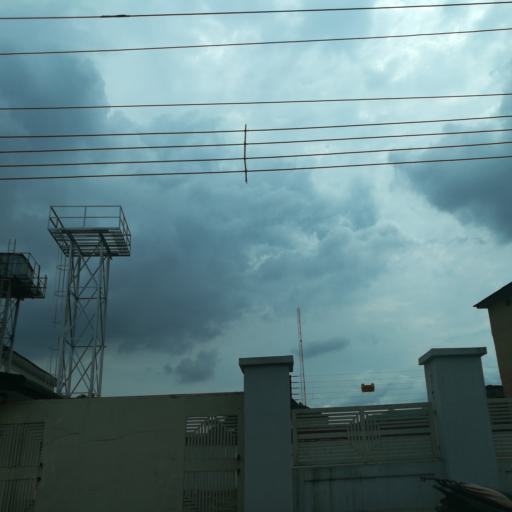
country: NG
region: Rivers
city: Port Harcourt
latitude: 4.8254
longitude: 7.0006
